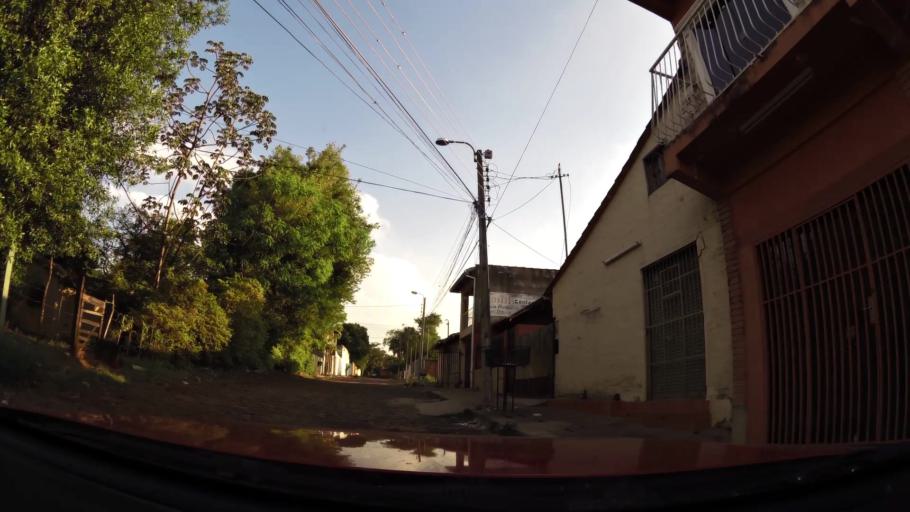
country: PY
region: Central
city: San Lorenzo
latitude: -25.3564
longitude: -57.5164
